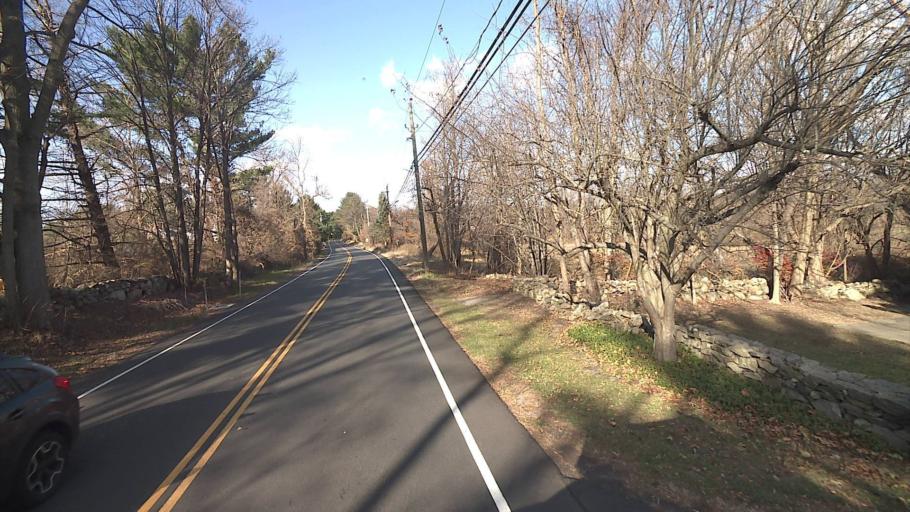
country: US
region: Connecticut
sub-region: Fairfield County
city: Wilton
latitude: 41.1852
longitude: -73.3957
